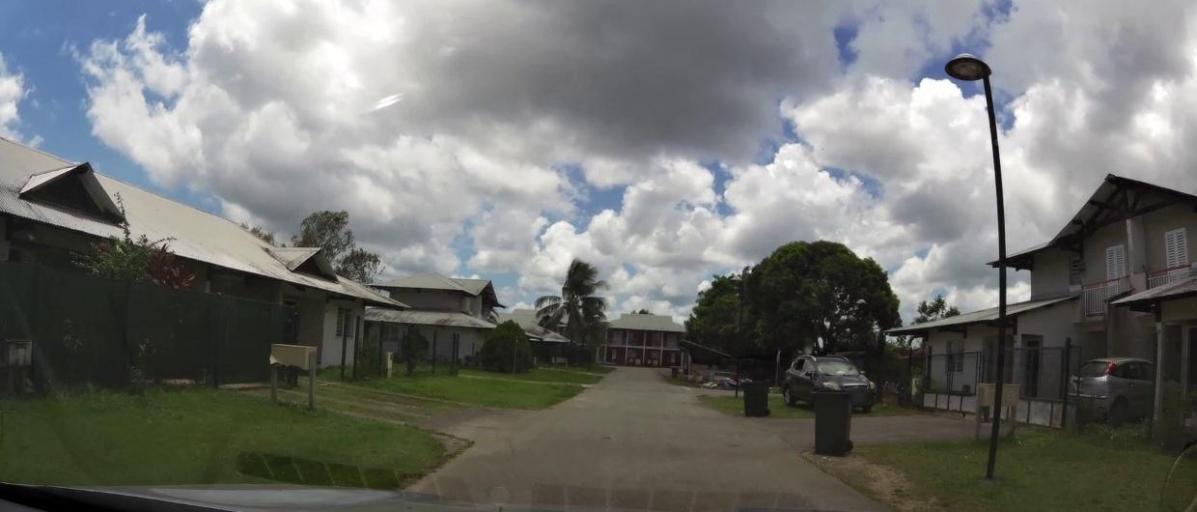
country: GF
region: Guyane
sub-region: Guyane
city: Sinnamary
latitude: 5.3757
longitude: -52.9547
